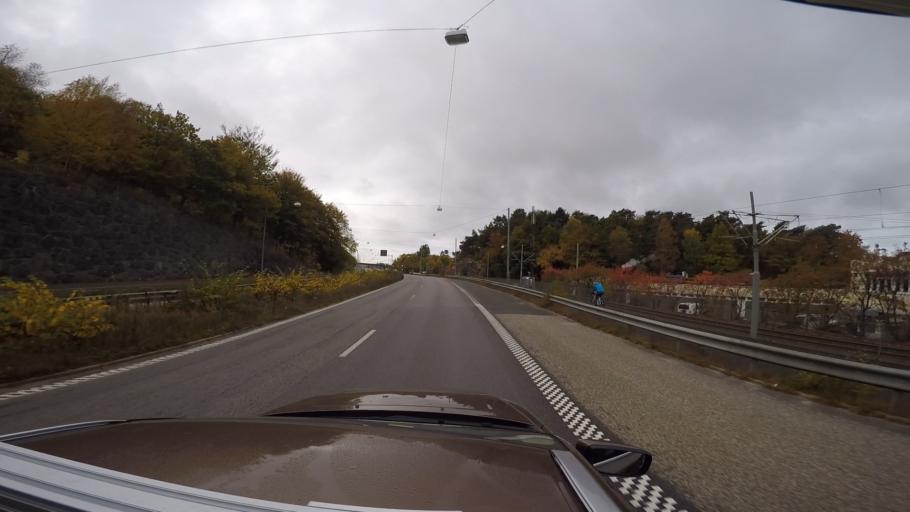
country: SE
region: Vaestra Goetaland
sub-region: Goteborg
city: Majorna
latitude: 57.6768
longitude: 11.9407
